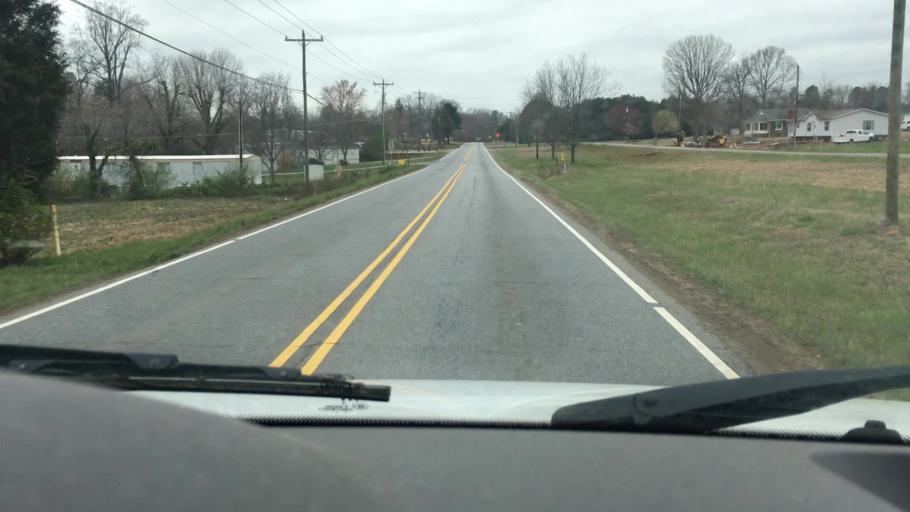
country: US
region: North Carolina
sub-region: Iredell County
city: Troutman
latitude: 35.6893
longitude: -80.8670
